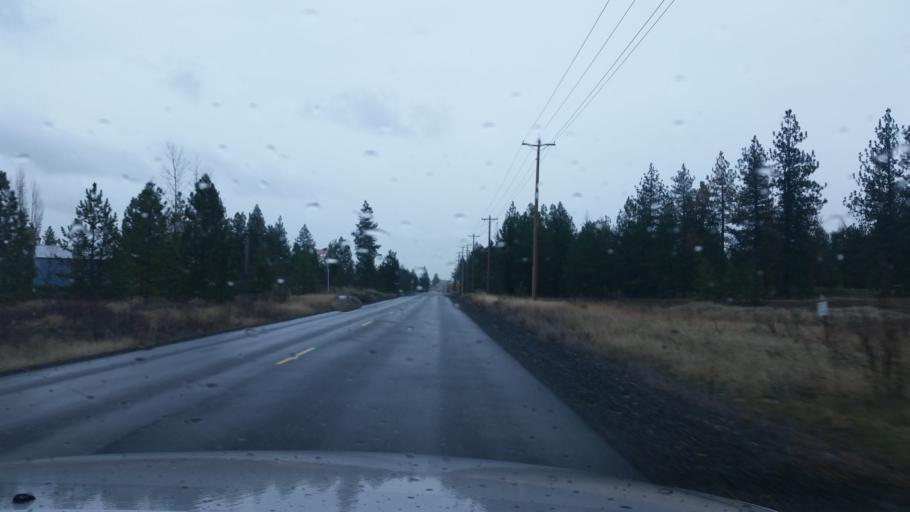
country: US
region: Washington
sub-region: Spokane County
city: Airway Heights
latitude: 47.6719
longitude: -117.5890
